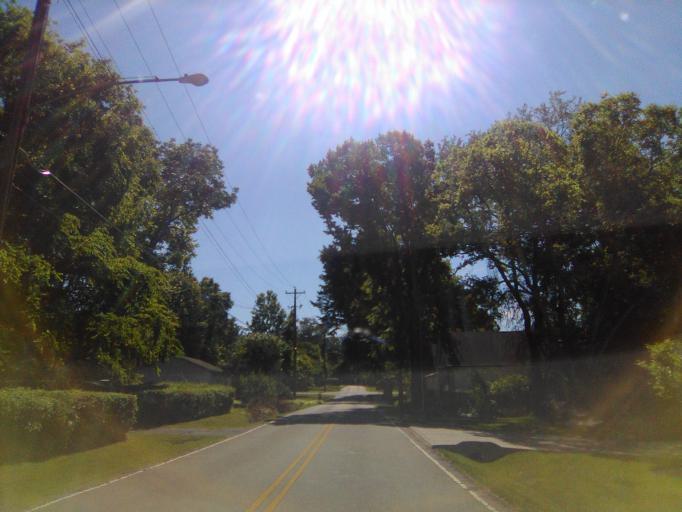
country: US
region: Tennessee
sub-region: Davidson County
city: Belle Meade
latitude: 36.1220
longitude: -86.8332
